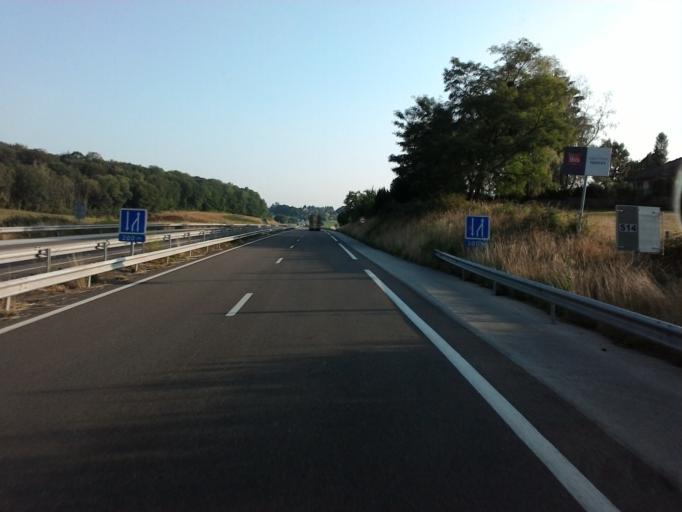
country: FR
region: Franche-Comte
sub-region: Departement de la Haute-Saone
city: Echenoz-la-Meline
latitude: 47.5686
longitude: 6.1400
